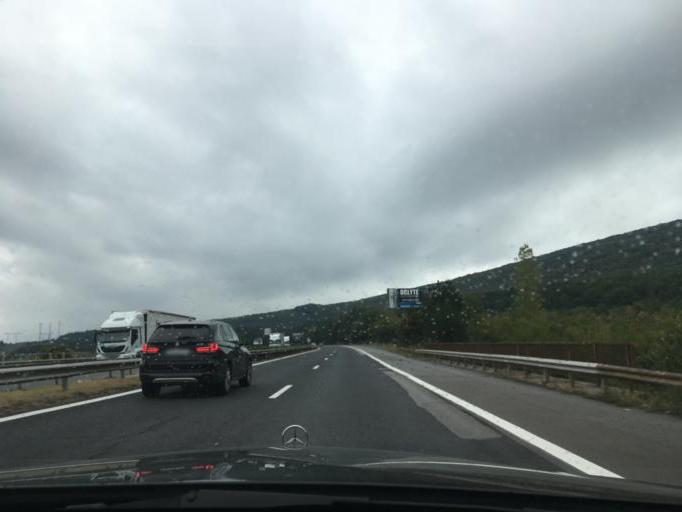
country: BG
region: Sofiya
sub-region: Obshtina Elin Pelin
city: Elin Pelin
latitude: 42.6001
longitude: 23.5661
